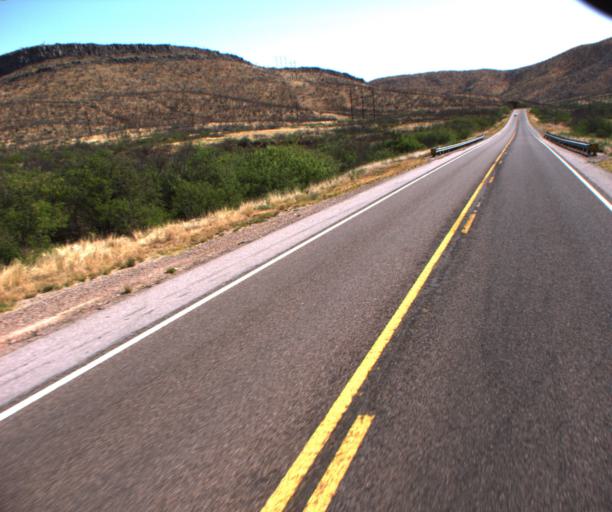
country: US
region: Arizona
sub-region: Cochise County
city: Bisbee
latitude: 31.4319
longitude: -109.8512
